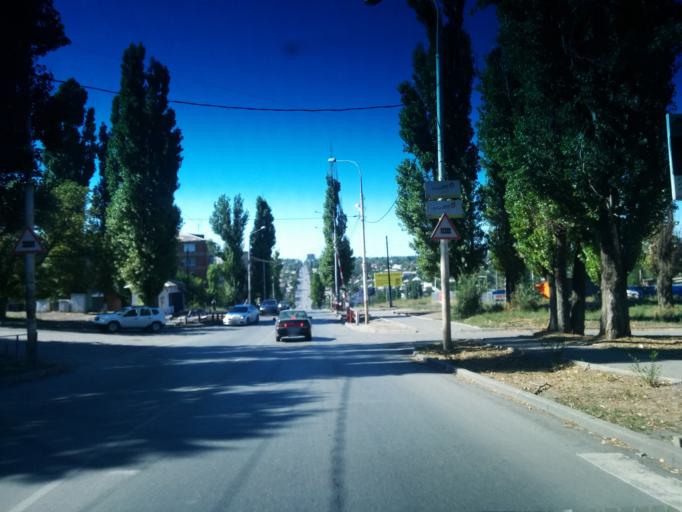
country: RU
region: Rostov
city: Shakhty
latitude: 47.6956
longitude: 40.2429
